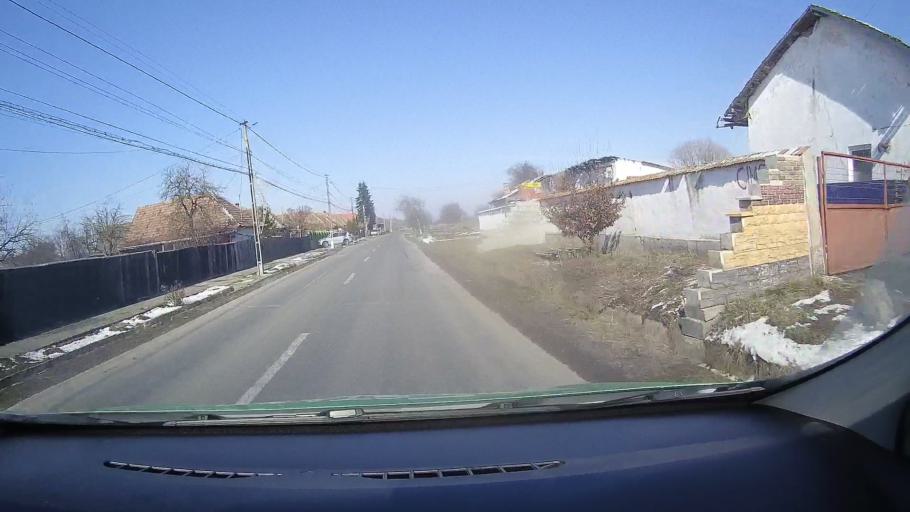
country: RO
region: Brasov
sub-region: Comuna Homorod
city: Homorod
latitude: 46.0209
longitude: 25.2745
